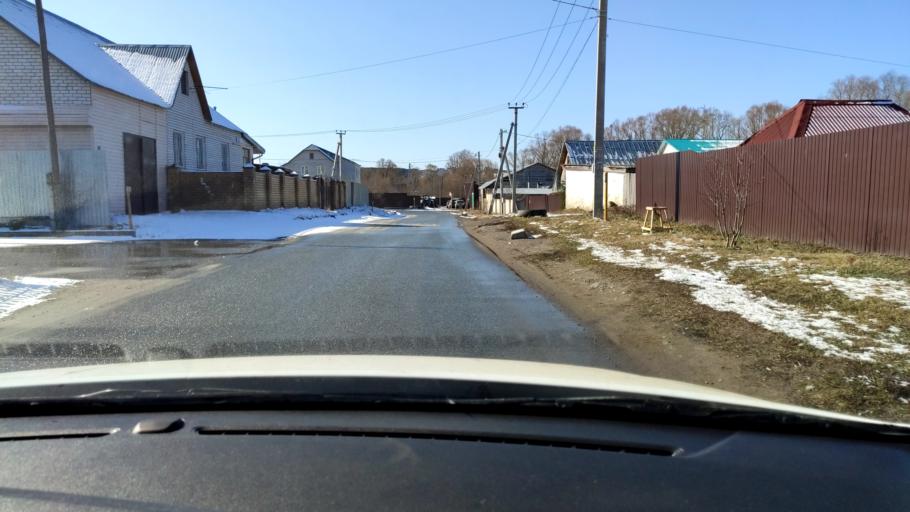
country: RU
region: Tatarstan
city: Vysokaya Gora
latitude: 55.8725
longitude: 49.2437
